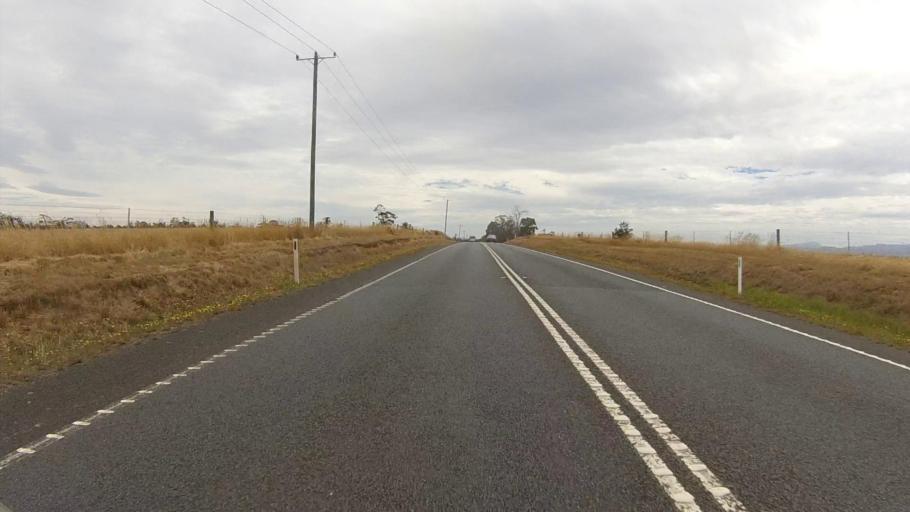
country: AU
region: Tasmania
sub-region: Northern Midlands
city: Evandale
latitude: -41.7080
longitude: 147.2991
